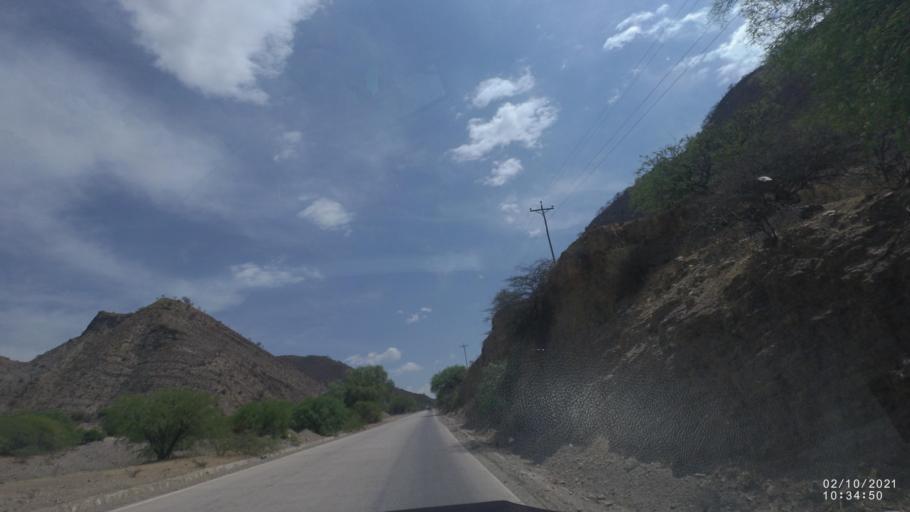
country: BO
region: Cochabamba
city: Capinota
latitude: -17.6690
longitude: -66.2572
